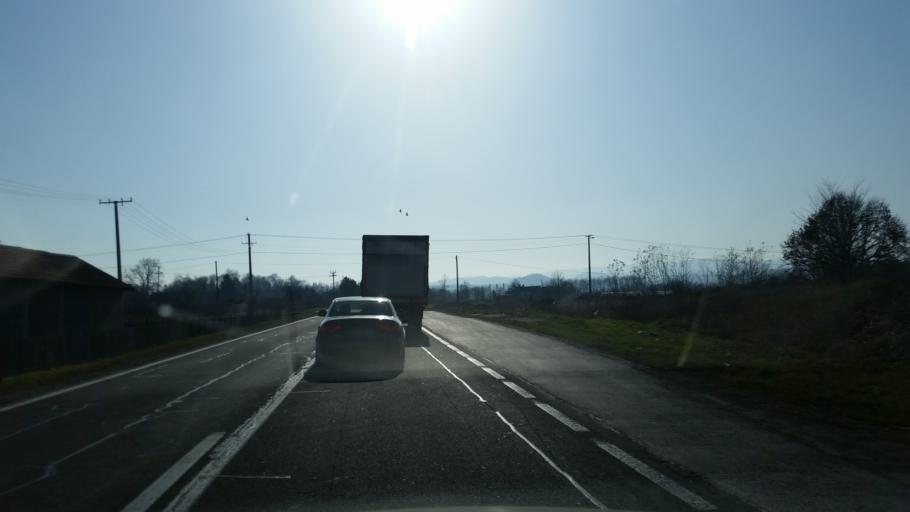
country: RS
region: Central Serbia
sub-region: Kolubarski Okrug
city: Ljig
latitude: 44.2718
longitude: 20.2834
